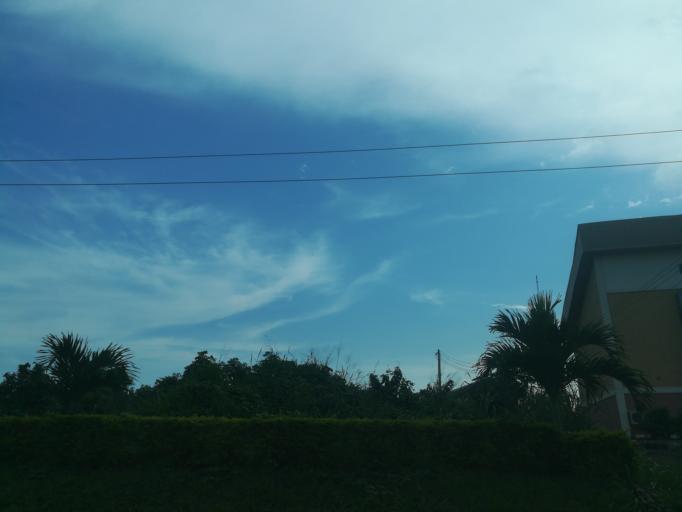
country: NG
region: Lagos
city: Ikorodu
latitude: 6.6359
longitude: 3.5361
